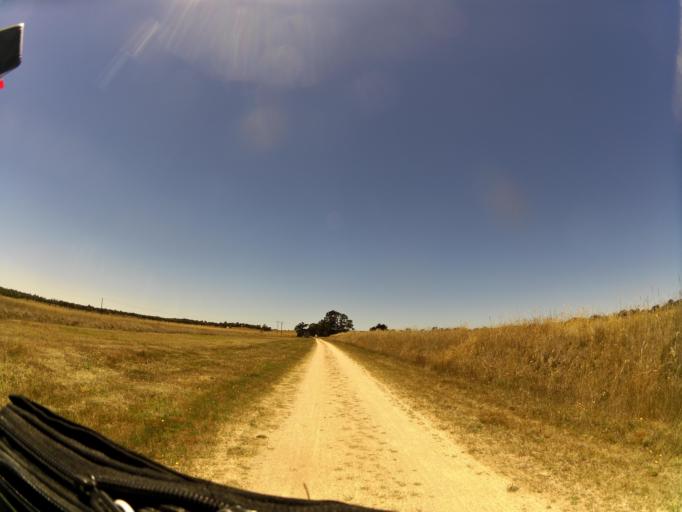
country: AU
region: Victoria
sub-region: Ballarat North
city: Delacombe
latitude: -37.5628
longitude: 143.7352
